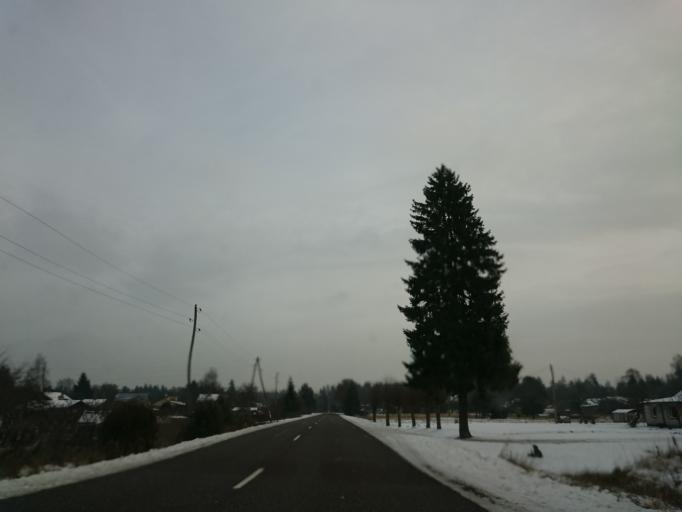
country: LV
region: Saulkrastu
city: Saulkrasti
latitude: 57.2386
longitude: 24.4661
